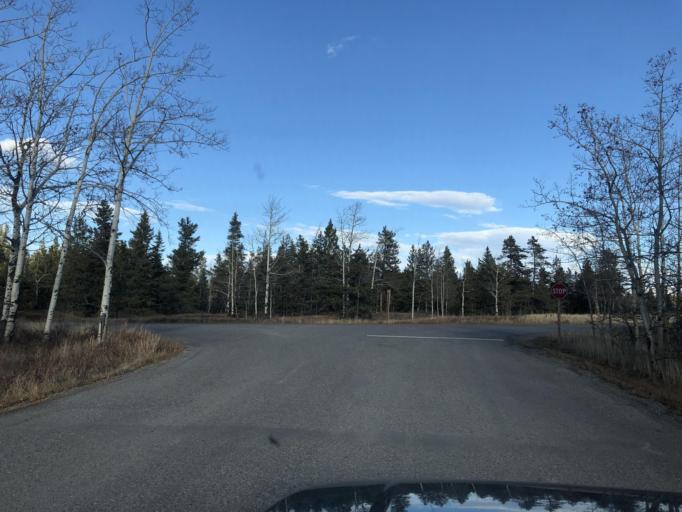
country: CA
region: Alberta
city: Canmore
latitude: 51.0728
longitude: -115.0757
